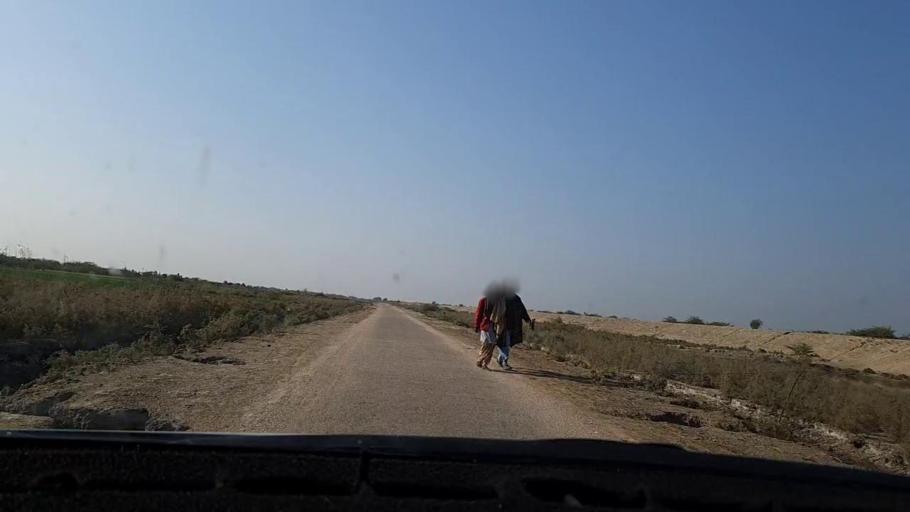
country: PK
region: Sindh
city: Tando Mittha Khan
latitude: 25.8331
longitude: 69.3163
